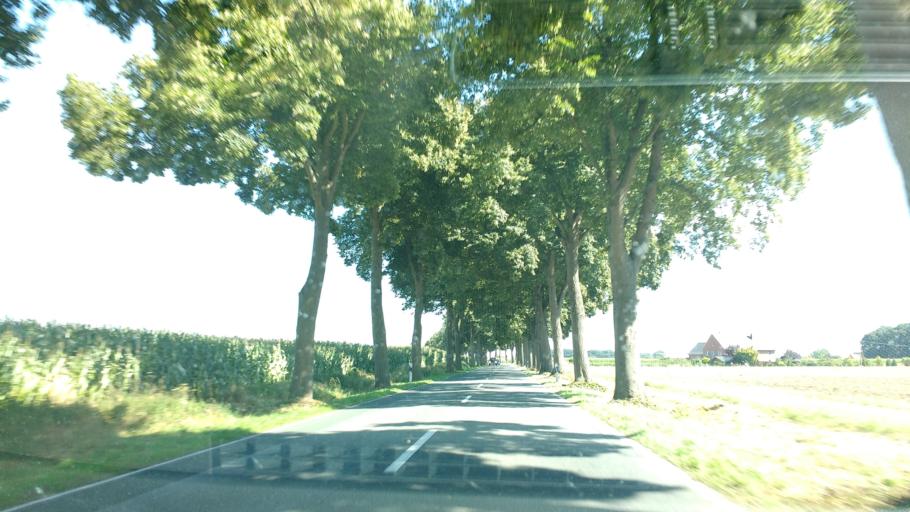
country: DE
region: North Rhine-Westphalia
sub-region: Regierungsbezirk Detmold
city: Langenberg
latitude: 51.8070
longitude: 8.3408
